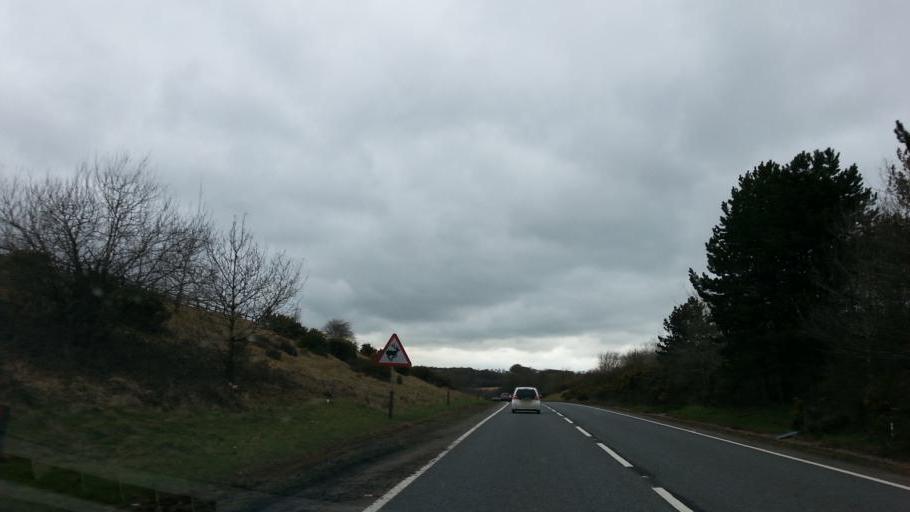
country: GB
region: England
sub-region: Devon
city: Tiverton
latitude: 50.9674
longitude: -3.6204
